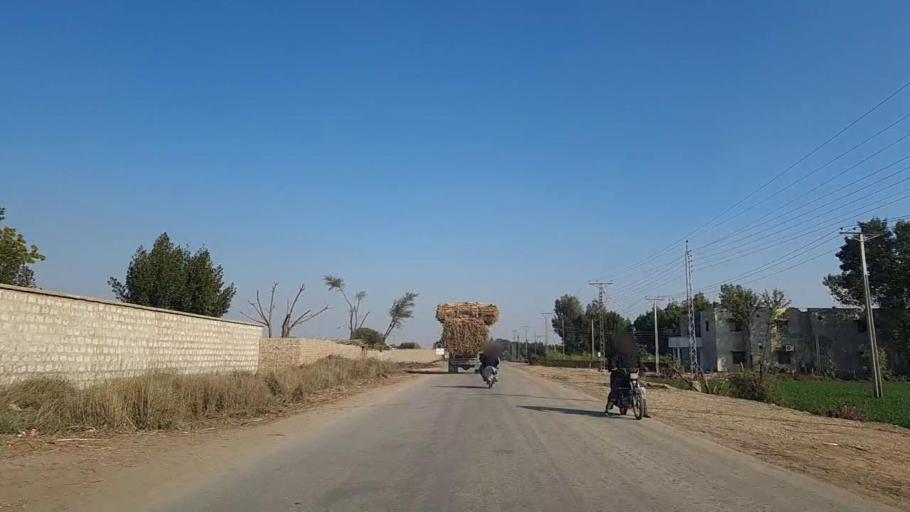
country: PK
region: Sindh
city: Bandhi
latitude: 26.6051
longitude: 68.3137
